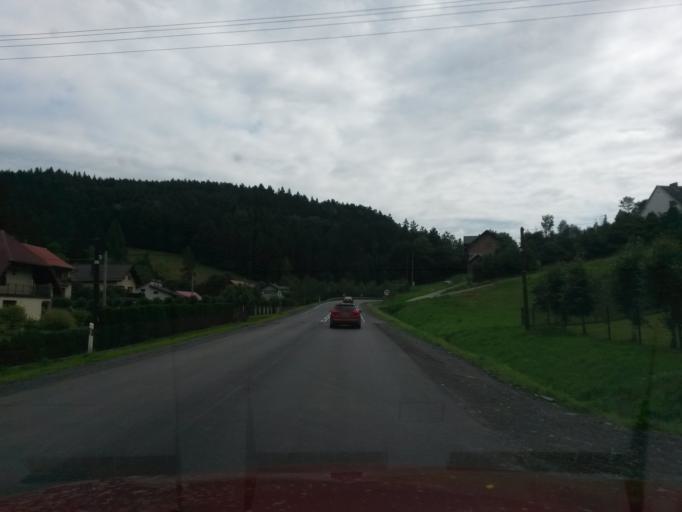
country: PL
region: Lesser Poland Voivodeship
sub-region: Powiat nowosadecki
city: Labowa
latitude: 49.4889
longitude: 20.9137
